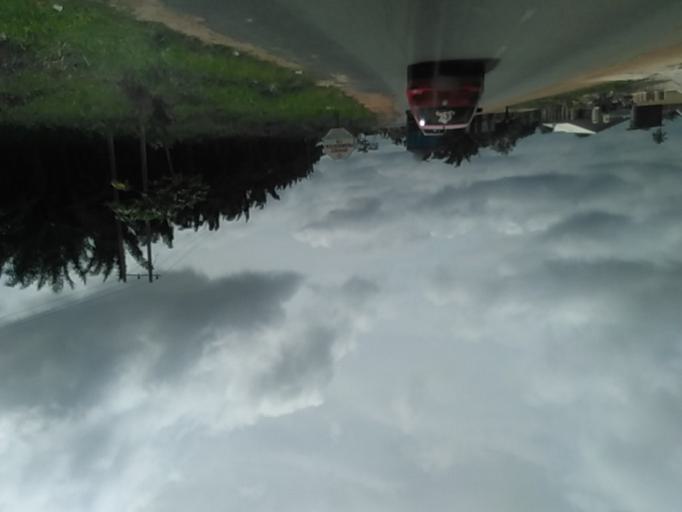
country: GH
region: Ashanti
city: Mamponteng
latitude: 6.7662
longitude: -1.4558
